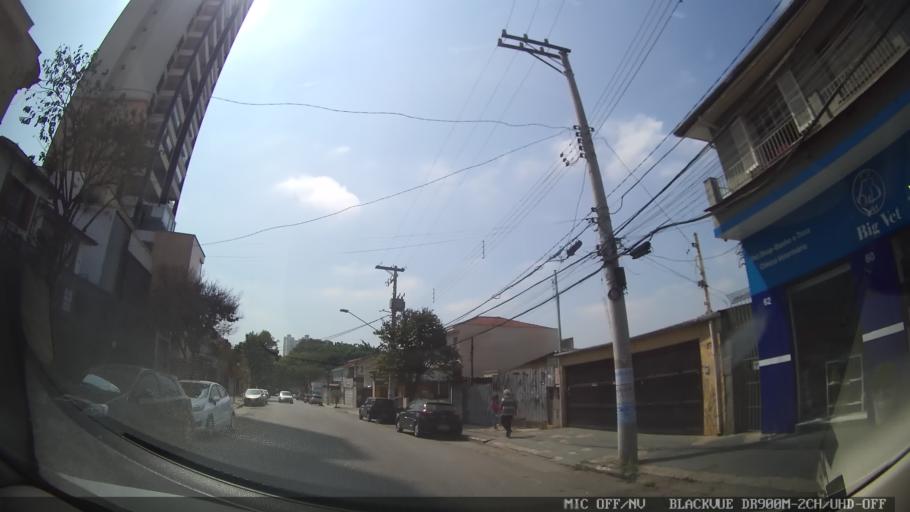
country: BR
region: Sao Paulo
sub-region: Sao Paulo
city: Sao Paulo
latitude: -23.5025
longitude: -46.6720
